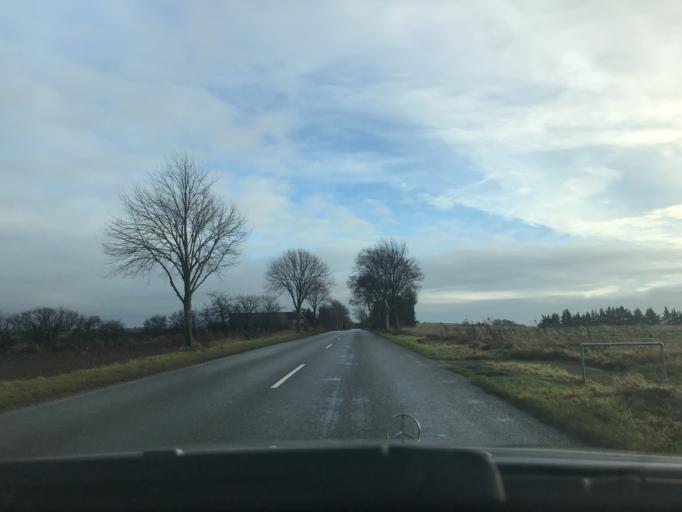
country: DK
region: South Denmark
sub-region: Sonderborg Kommune
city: Broager
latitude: 54.8862
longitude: 9.6900
